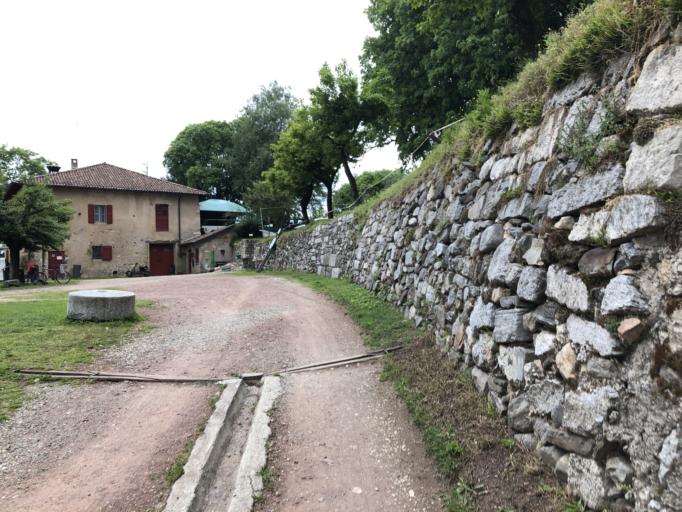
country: IT
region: Piedmont
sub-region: Provincia di Novara
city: Arona
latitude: 45.7640
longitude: 8.5548
